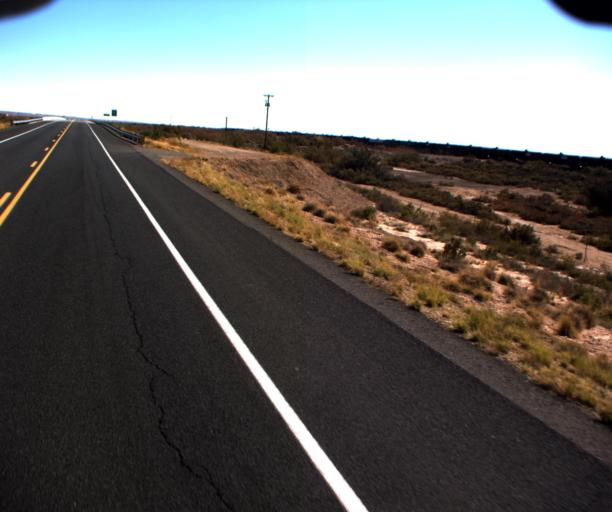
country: US
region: Arizona
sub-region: Navajo County
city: Winslow
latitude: 35.0070
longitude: -110.6561
